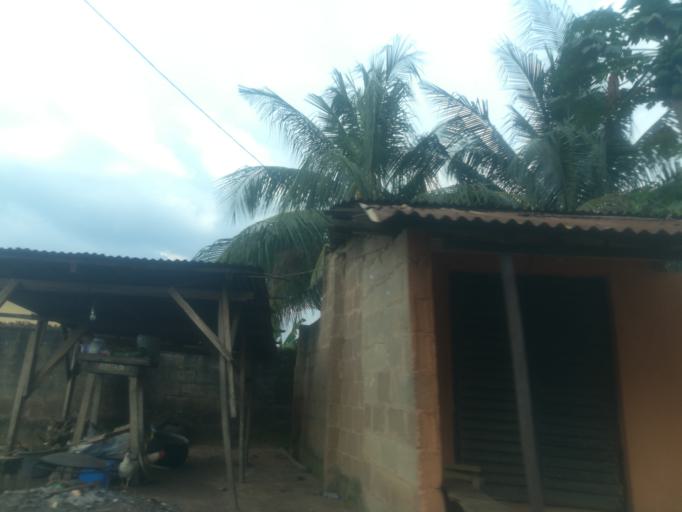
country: NG
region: Oyo
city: Ibadan
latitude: 7.4067
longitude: 3.8299
